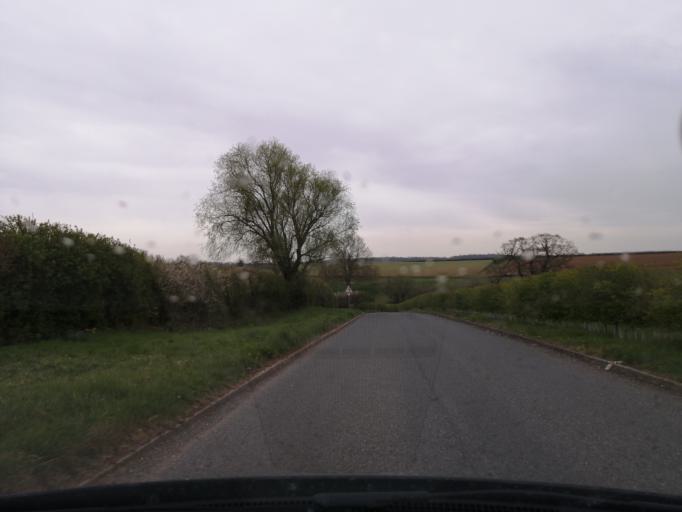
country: GB
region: England
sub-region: Peterborough
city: Wittering
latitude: 52.6104
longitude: -0.4534
